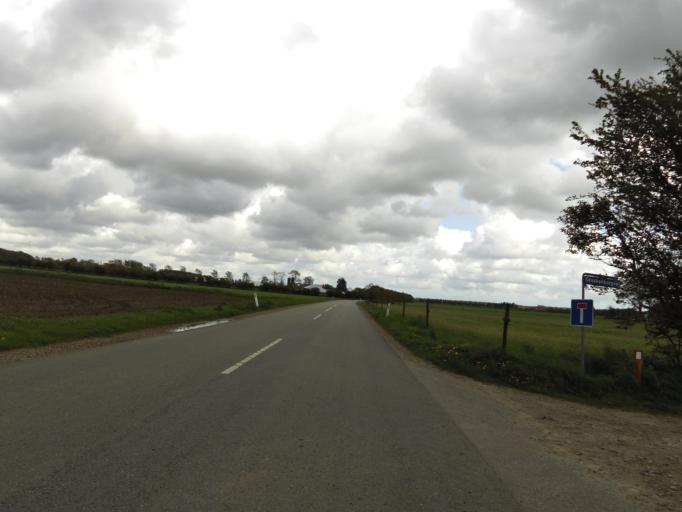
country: DK
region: South Denmark
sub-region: Haderslev Kommune
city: Gram
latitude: 55.3109
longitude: 8.9909
